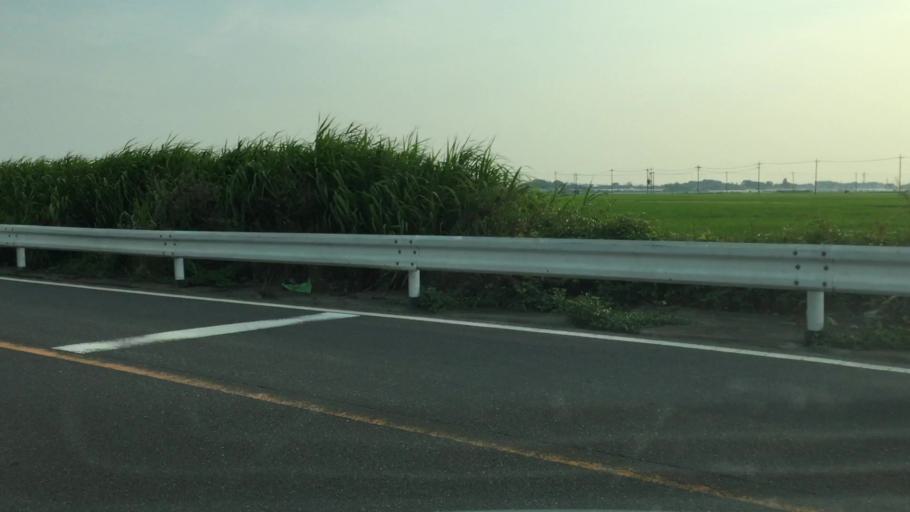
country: JP
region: Tochigi
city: Fujioka
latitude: 36.2485
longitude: 139.5967
